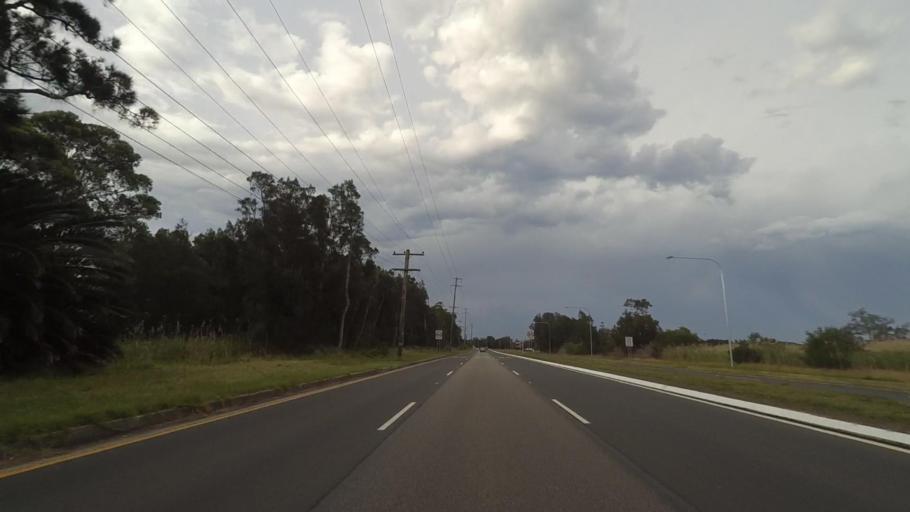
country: AU
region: New South Wales
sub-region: Shellharbour
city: Lake Illawarra
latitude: -34.5230
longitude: 150.8700
